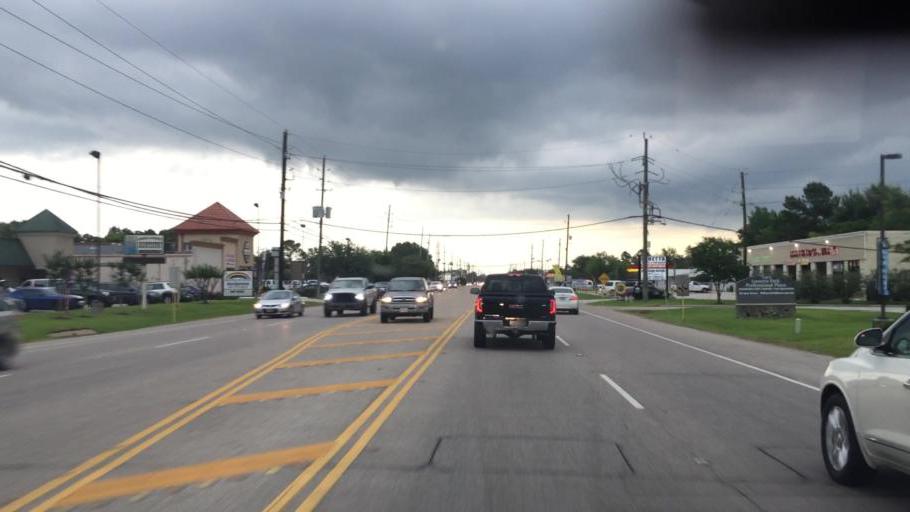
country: US
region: Texas
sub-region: Harris County
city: Spring
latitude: 30.0367
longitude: -95.4952
